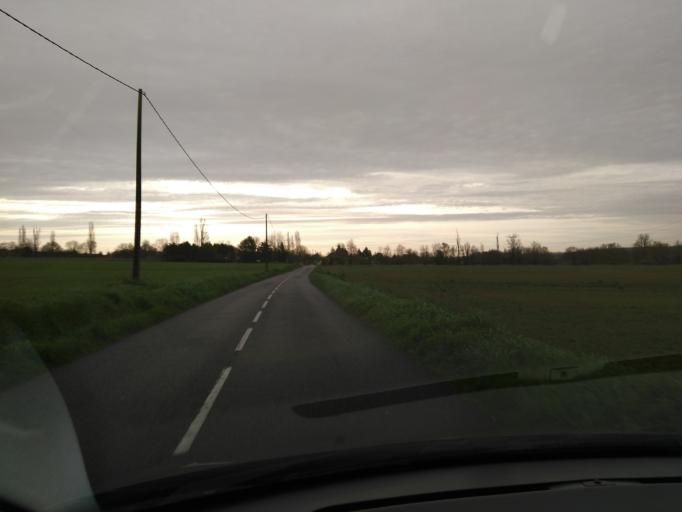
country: FR
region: Midi-Pyrenees
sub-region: Departement de la Haute-Garonne
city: Labastide-Saint-Sernin
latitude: 43.7514
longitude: 1.4636
